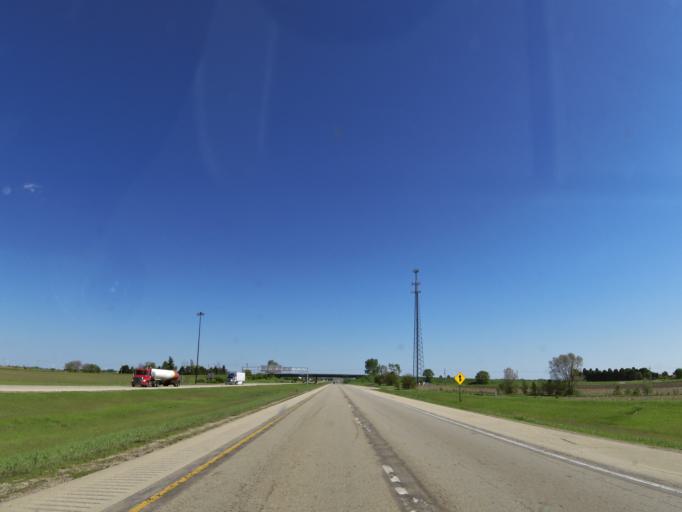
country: US
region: Illinois
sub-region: Ogle County
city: Rochelle
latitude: 41.9017
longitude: -89.0194
